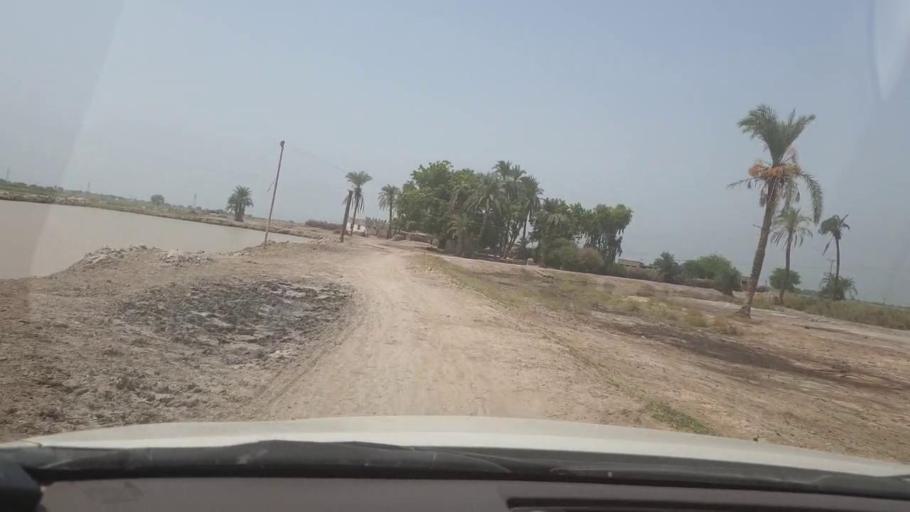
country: PK
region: Sindh
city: Shikarpur
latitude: 27.9621
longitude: 68.5906
